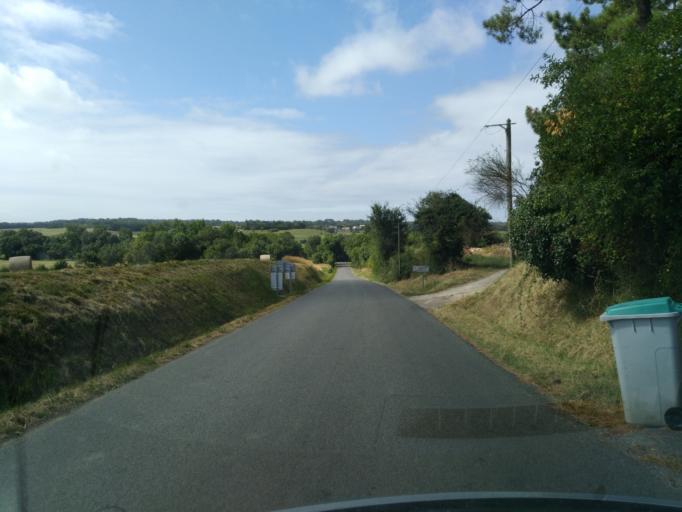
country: FR
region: Poitou-Charentes
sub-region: Departement de la Charente-Maritime
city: Breuillet
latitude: 45.6853
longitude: -1.0778
